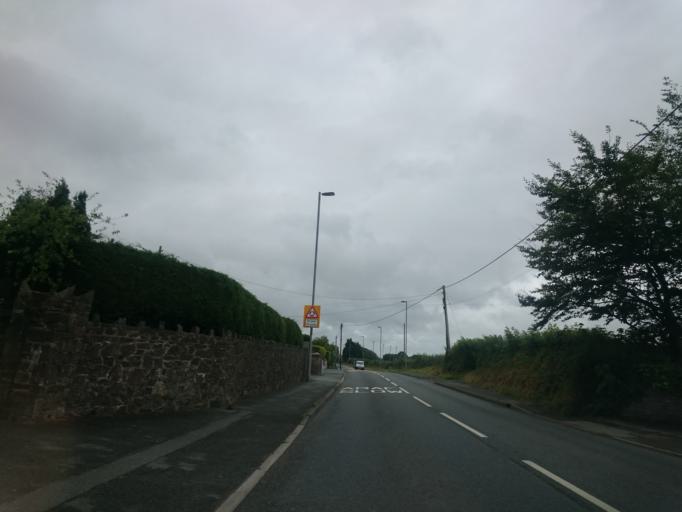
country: GB
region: Wales
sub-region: Pembrokeshire
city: Haverfordwest
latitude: 51.7865
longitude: -4.9748
